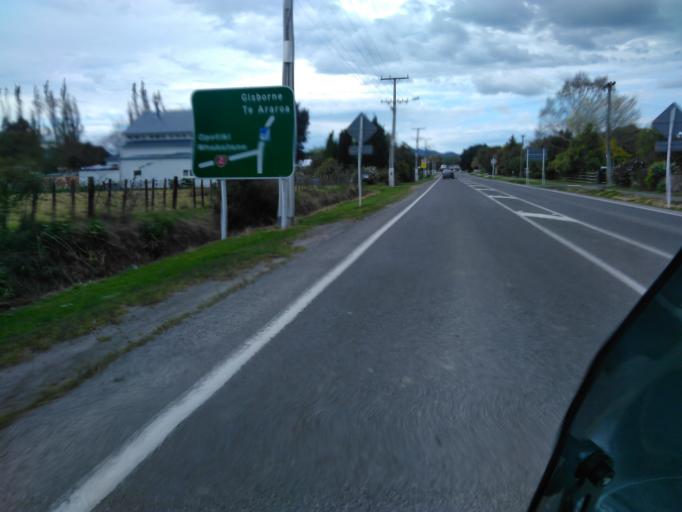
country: NZ
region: Gisborne
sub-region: Gisborne District
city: Gisborne
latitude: -38.6513
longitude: 177.9611
